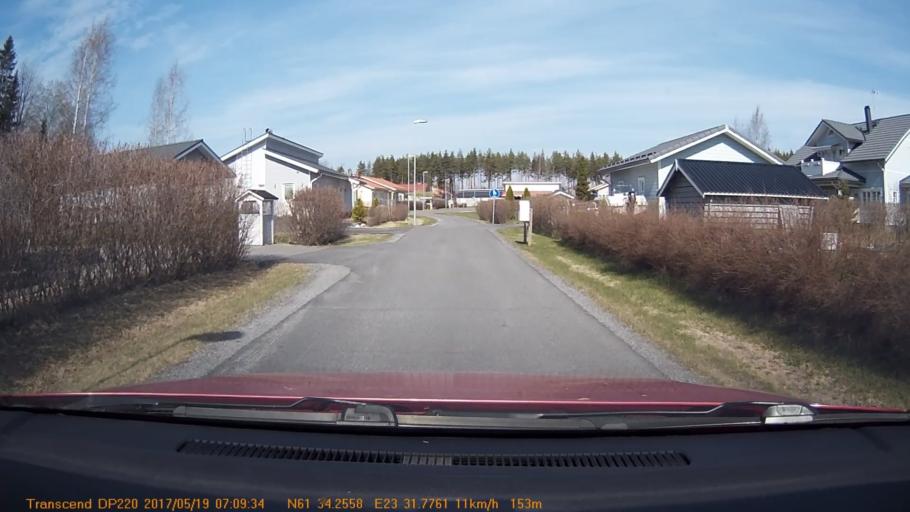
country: FI
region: Pirkanmaa
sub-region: Tampere
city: Yloejaervi
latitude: 61.5709
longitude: 23.5296
